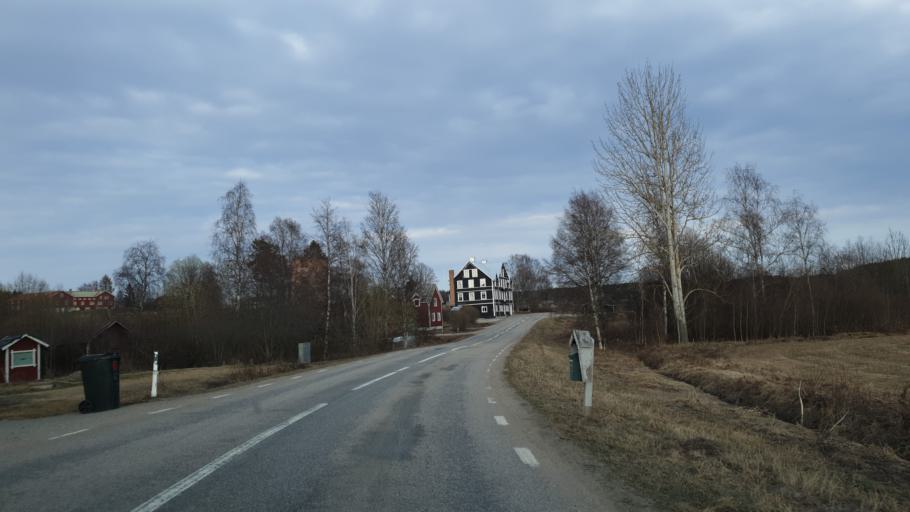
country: SE
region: Gaevleborg
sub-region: Nordanstigs Kommun
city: Bergsjoe
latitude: 61.9789
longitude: 17.2646
